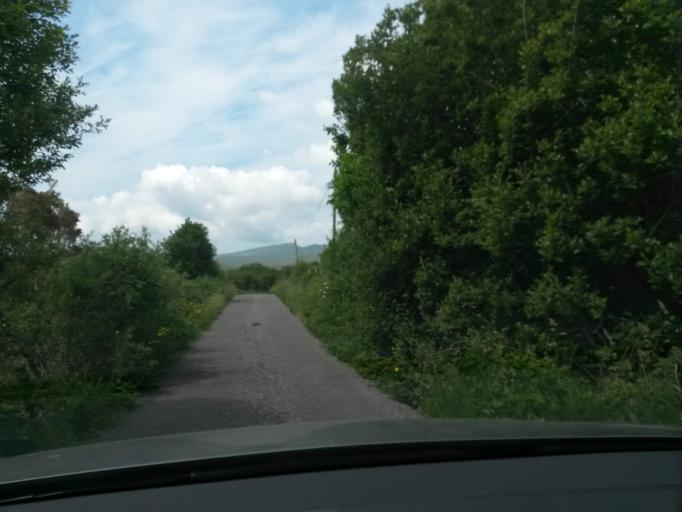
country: IE
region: Munster
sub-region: Ciarrai
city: Cahersiveen
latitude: 51.7988
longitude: -9.9594
